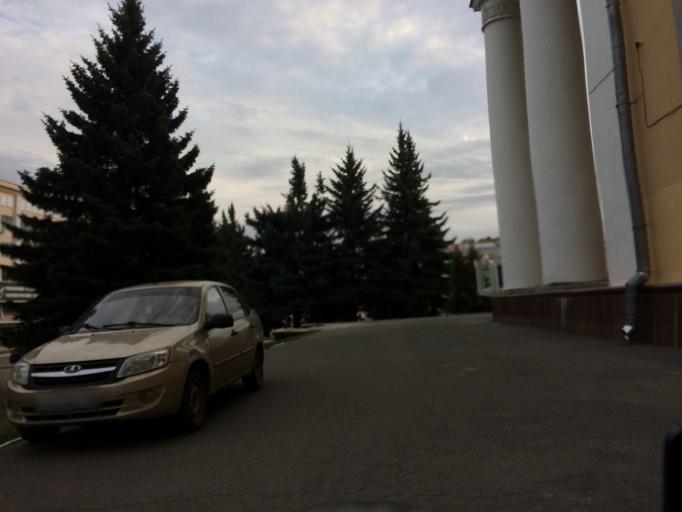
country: RU
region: Mariy-El
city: Yoshkar-Ola
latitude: 56.6317
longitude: 47.8919
